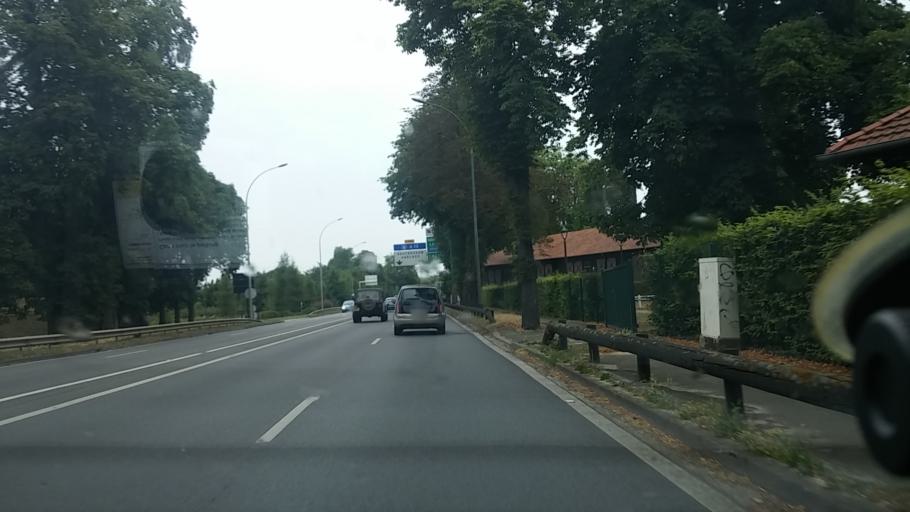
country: FR
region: Ile-de-France
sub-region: Departement des Hauts-de-Seine
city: Vaucresson
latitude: 48.8272
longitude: 2.1516
